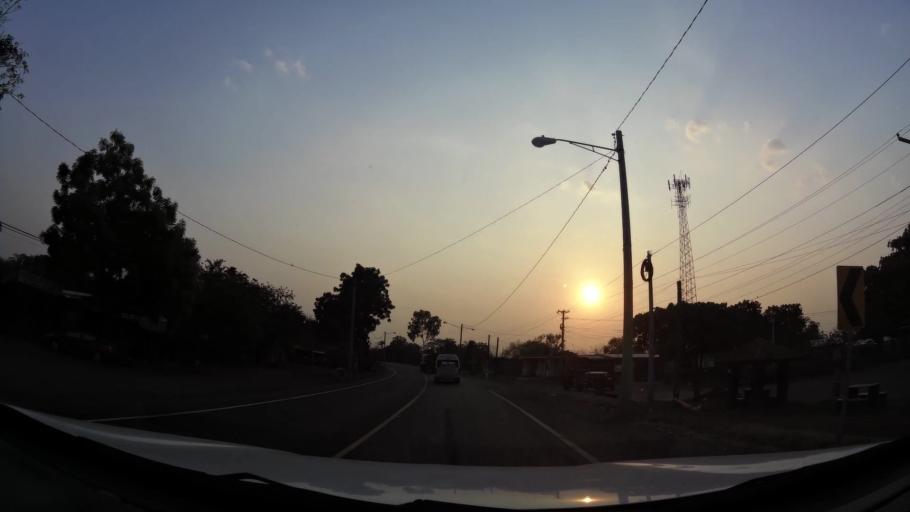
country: NI
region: Leon
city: La Paz Centro
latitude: 12.3347
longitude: -86.6786
